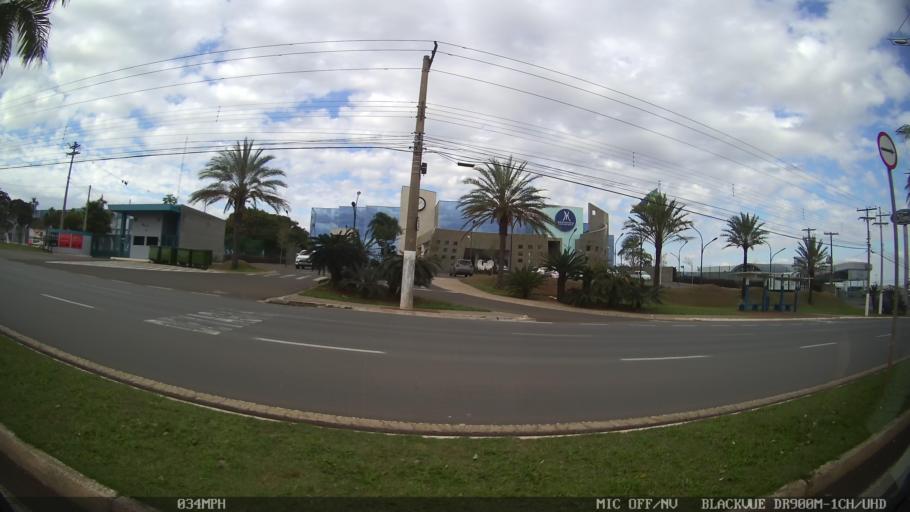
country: BR
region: Sao Paulo
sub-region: Limeira
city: Limeira
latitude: -22.5513
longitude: -47.3793
